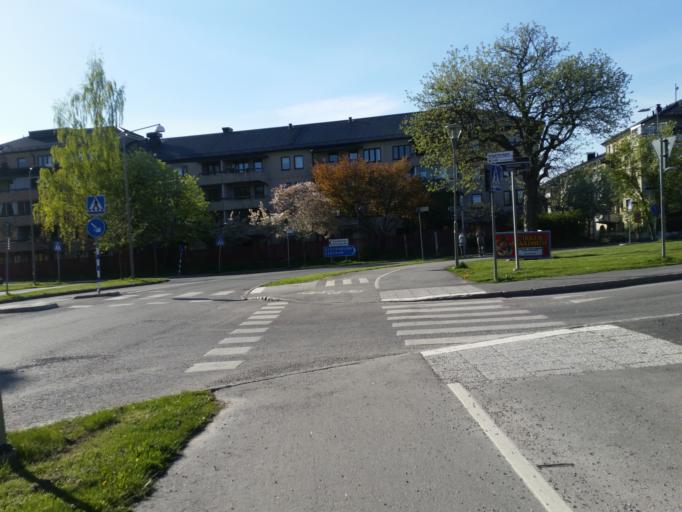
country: SE
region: Stockholm
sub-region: Stockholms Kommun
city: Arsta
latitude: 59.2843
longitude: 18.0991
